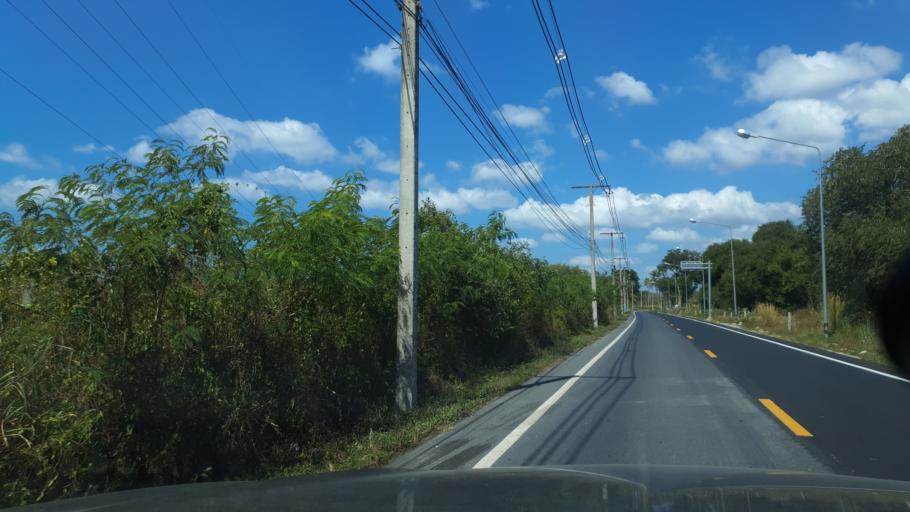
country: TH
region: Phuket
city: Thalang
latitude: 8.1517
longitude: 98.3054
